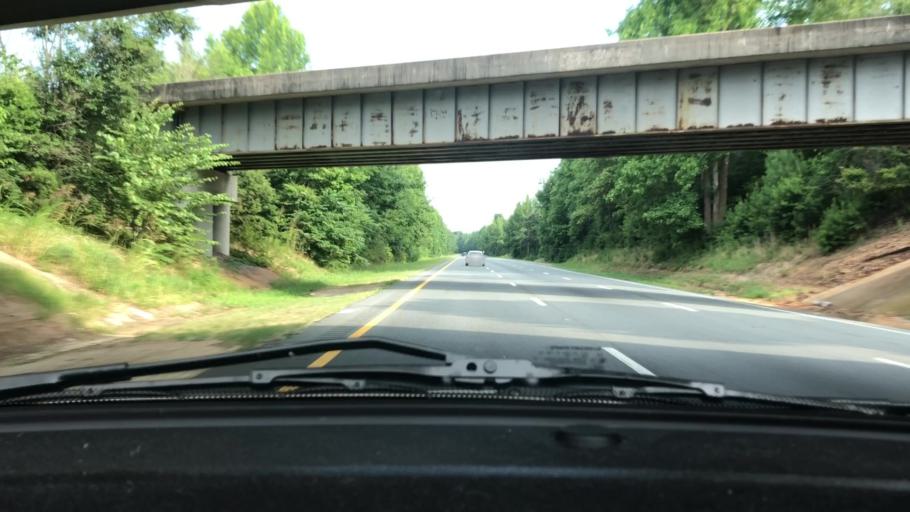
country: US
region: North Carolina
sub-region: Guilford County
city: Forest Oaks
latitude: 35.9144
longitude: -79.6752
